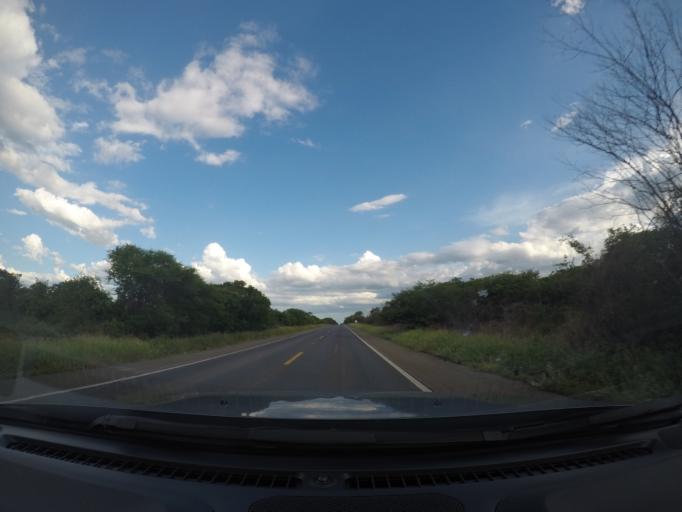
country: BR
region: Bahia
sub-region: Oliveira Dos Brejinhos
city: Beira Rio
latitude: -12.1992
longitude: -42.8146
